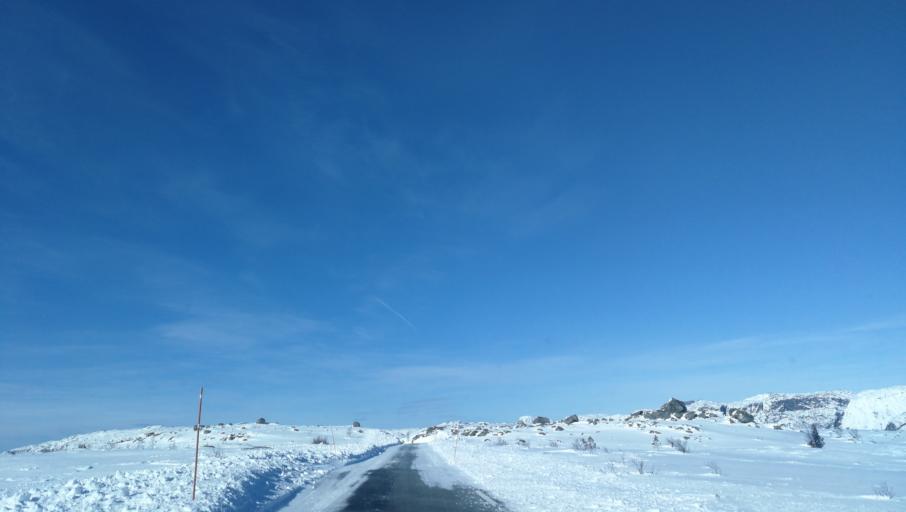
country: NO
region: Rogaland
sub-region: Hjelmeland
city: Hjelmelandsvagen
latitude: 59.1077
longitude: 6.3738
